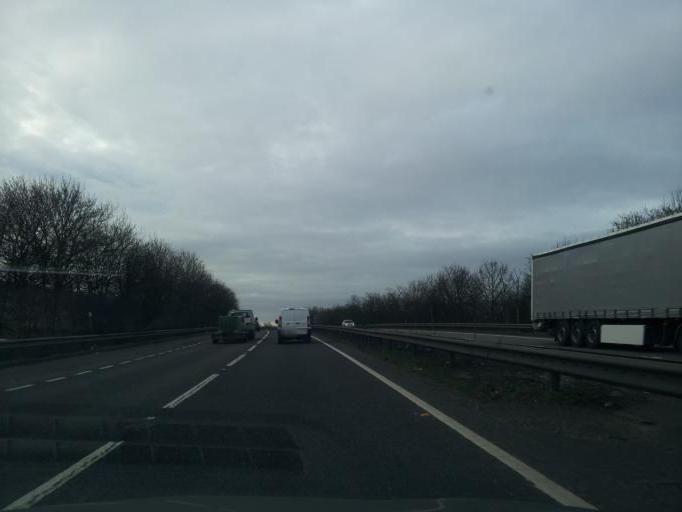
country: GB
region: England
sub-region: Lincolnshire
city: Great Gonerby
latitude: 52.9409
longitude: -0.6846
